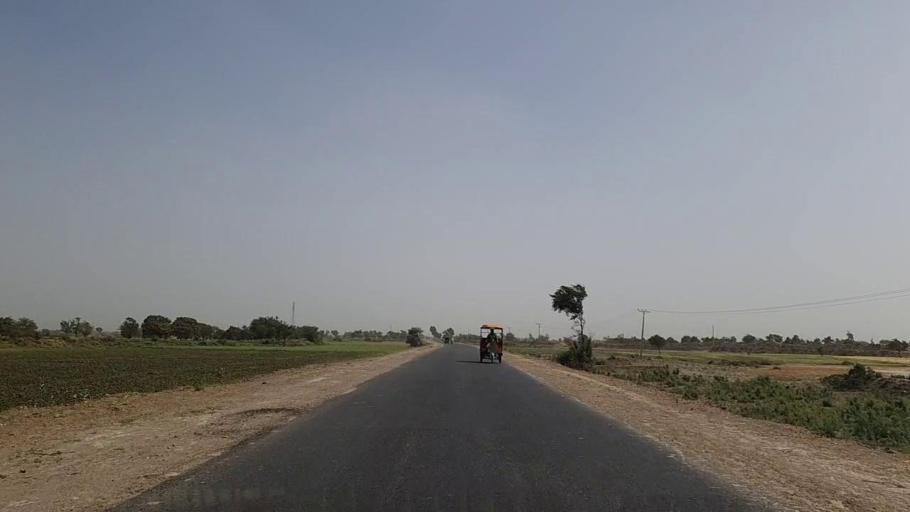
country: PK
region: Sindh
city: Tando Bago
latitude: 24.8320
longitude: 68.8925
